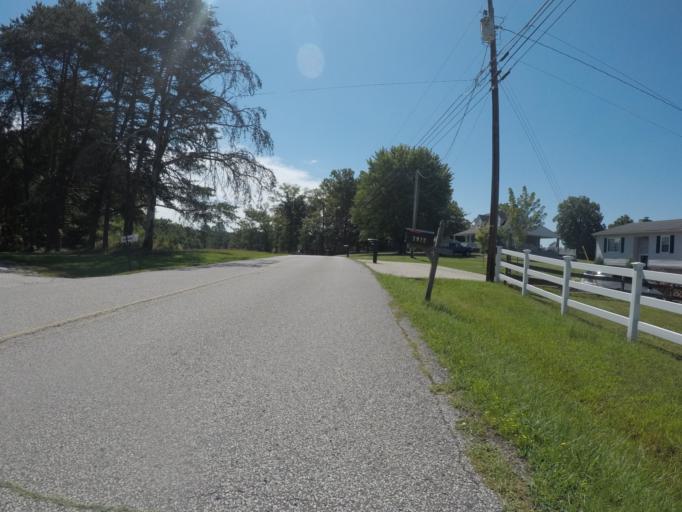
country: US
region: Kentucky
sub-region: Boyd County
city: Meads
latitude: 38.4124
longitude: -82.6582
